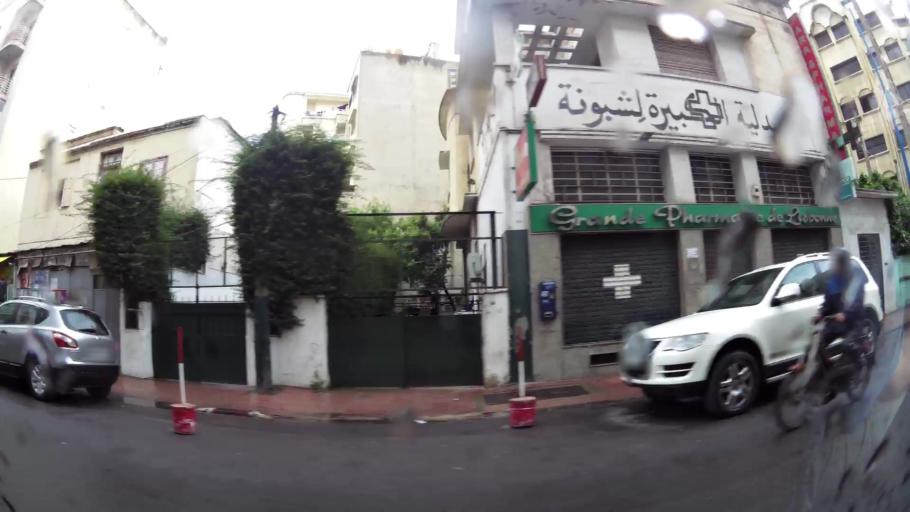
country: MA
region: Grand Casablanca
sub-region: Casablanca
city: Casablanca
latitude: 33.5752
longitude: -7.6136
